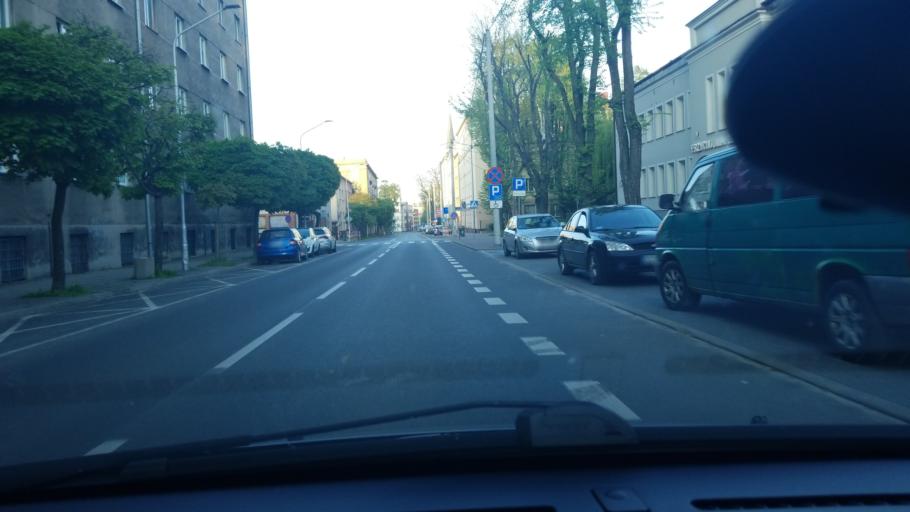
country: PL
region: Silesian Voivodeship
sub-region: Czestochowa
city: Czestochowa
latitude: 50.8084
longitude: 19.1089
